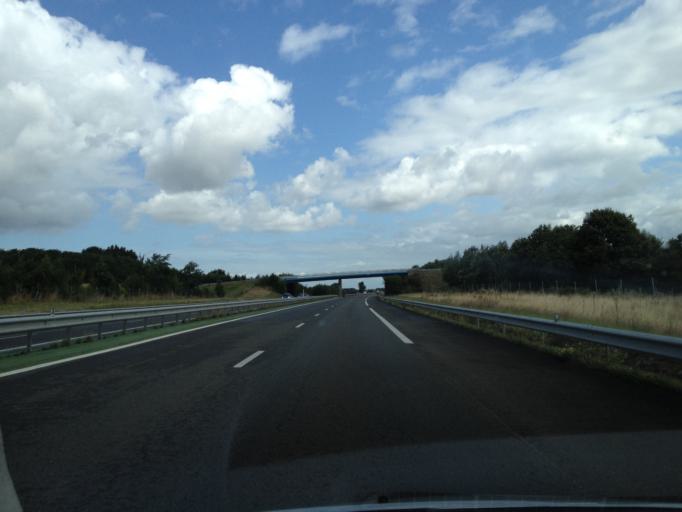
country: FR
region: Pays de la Loire
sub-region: Departement de Maine-et-Loire
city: Chemille-Melay
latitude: 47.1991
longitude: -0.7724
